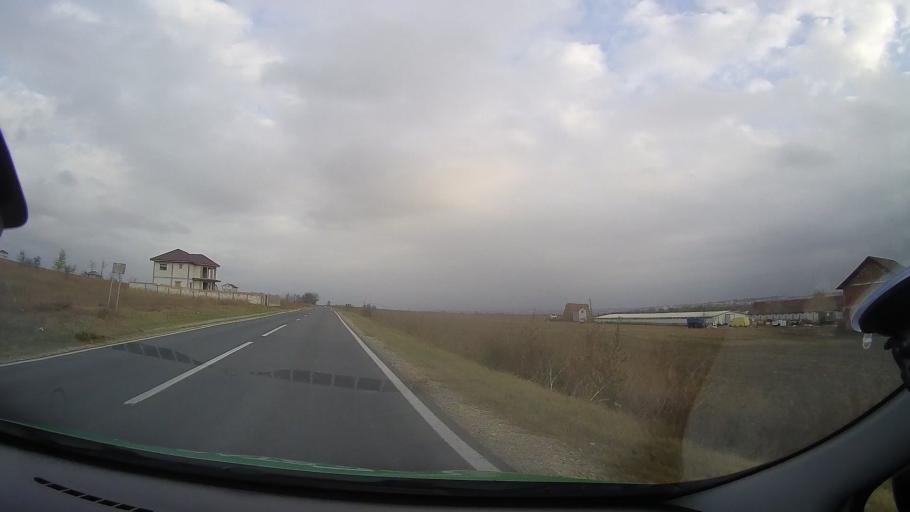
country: RO
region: Constanta
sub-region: Comuna Mircea Voda
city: Satu Nou
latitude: 44.2656
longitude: 28.2345
